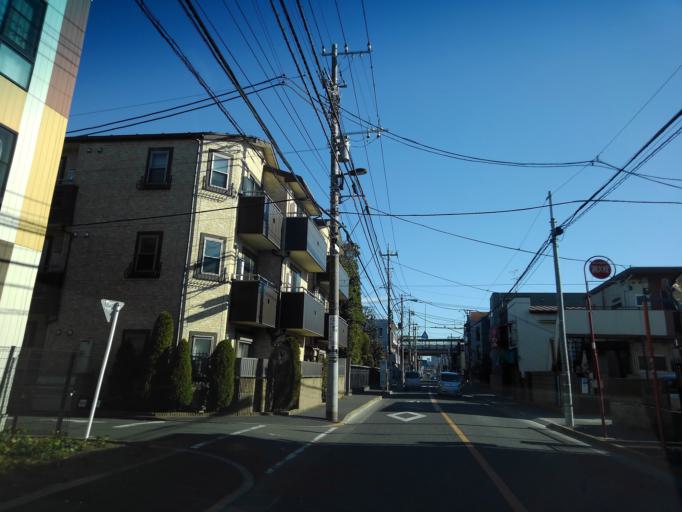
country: JP
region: Tokyo
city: Chofugaoka
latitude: 35.6594
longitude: 139.5285
